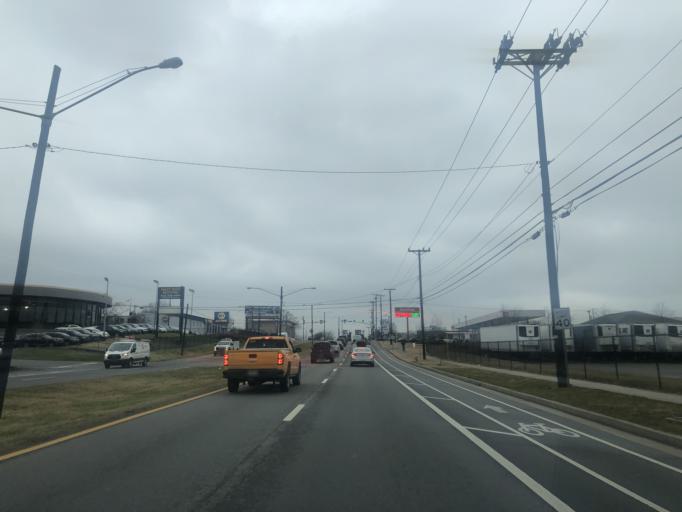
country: US
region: Tennessee
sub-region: Davidson County
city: Nashville
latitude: 36.1384
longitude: -86.7308
